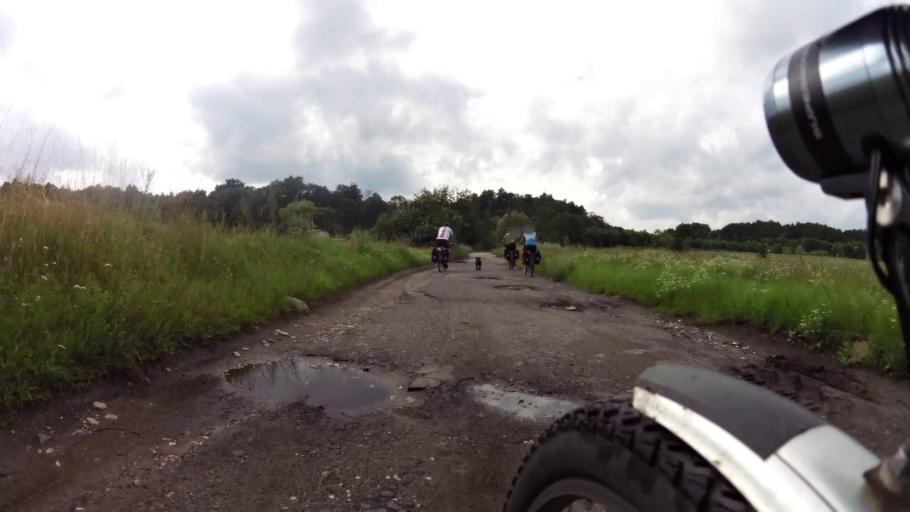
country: PL
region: West Pomeranian Voivodeship
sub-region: Powiat gryfinski
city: Banie
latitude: 53.1890
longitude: 14.5999
